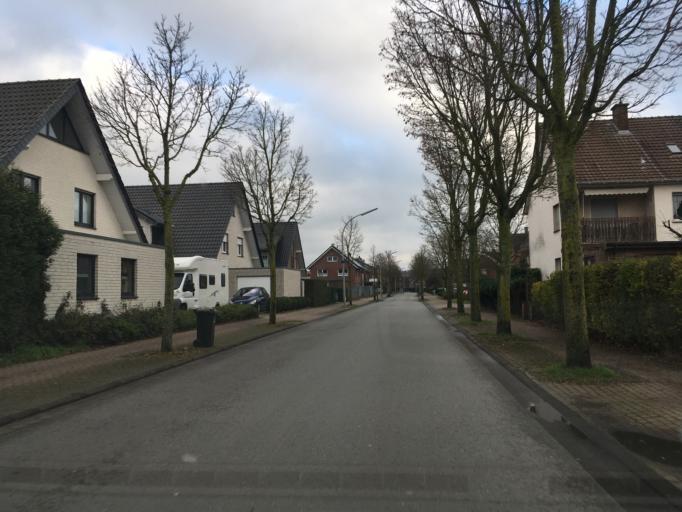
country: DE
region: North Rhine-Westphalia
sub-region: Regierungsbezirk Munster
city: Gescher
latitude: 51.9480
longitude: 7.0131
